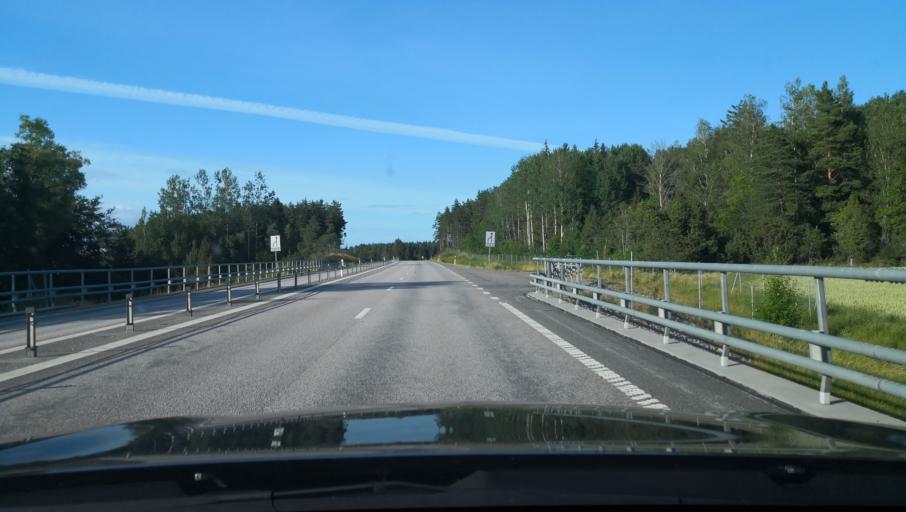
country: SE
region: Uppsala
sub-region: Uppsala Kommun
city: Vattholma
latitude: 59.9595
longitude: 17.8864
